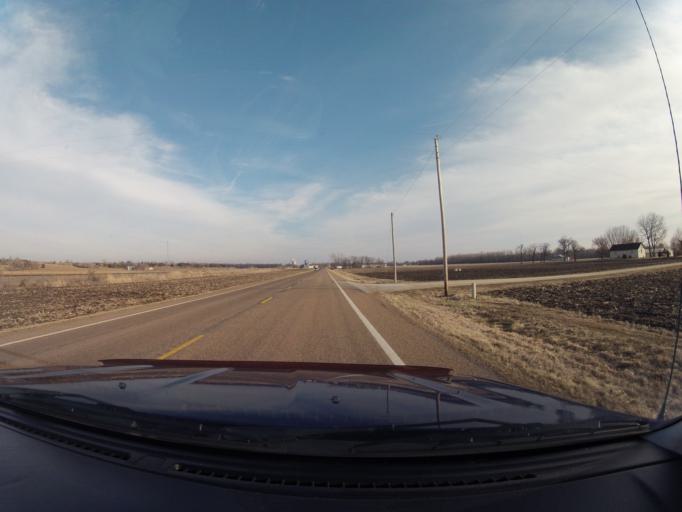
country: US
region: Kansas
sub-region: Pottawatomie County
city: Saint Marys
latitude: 39.2025
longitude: -96.0916
